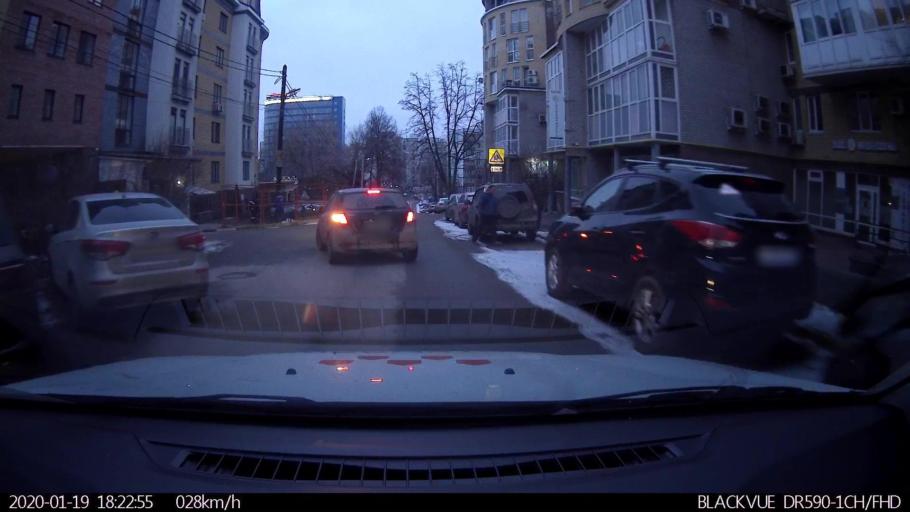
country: RU
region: Nizjnij Novgorod
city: Nizhniy Novgorod
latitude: 56.3229
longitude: 44.0306
